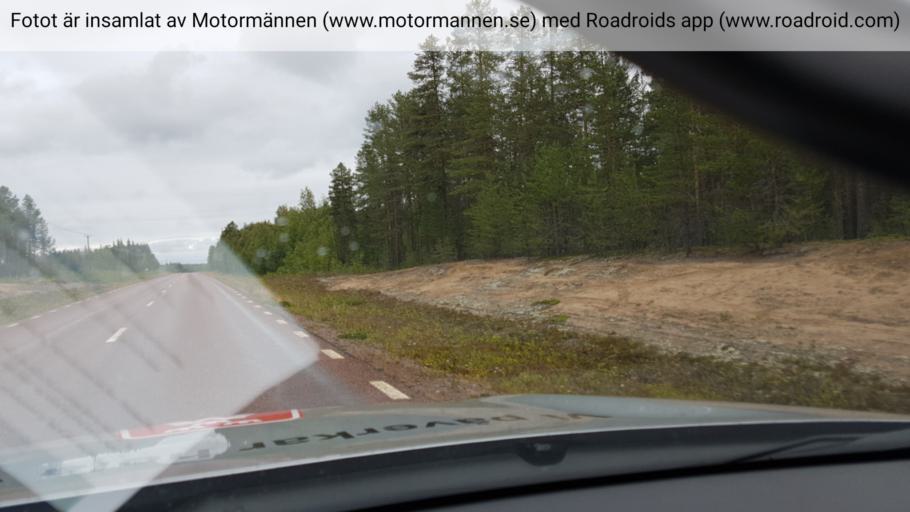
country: SE
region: Norrbotten
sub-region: Pajala Kommun
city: Pajala
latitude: 67.1216
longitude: 22.6057
